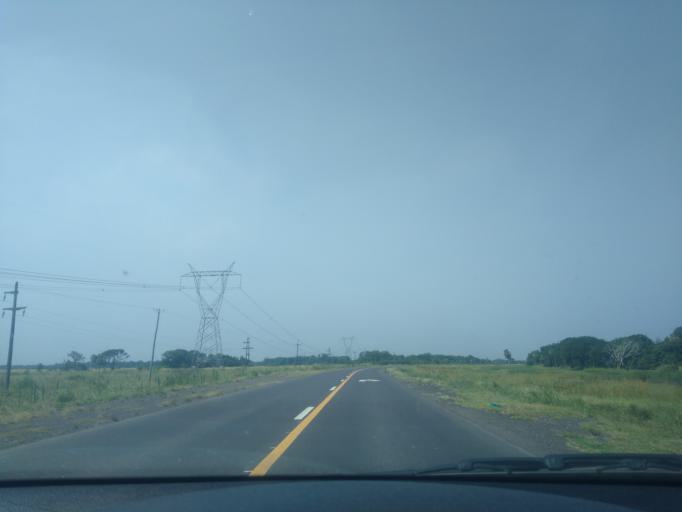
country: AR
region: Chaco
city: Fontana
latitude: -27.5592
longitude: -59.1489
